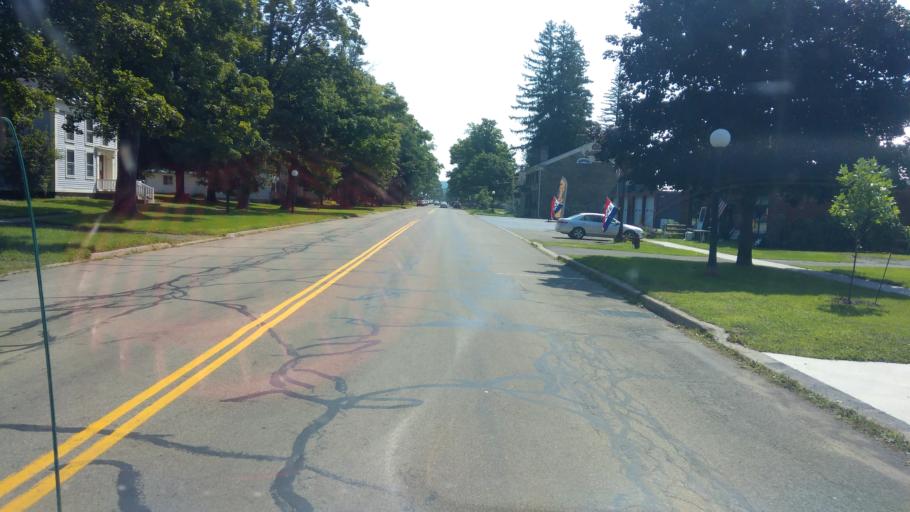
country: US
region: New York
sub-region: Allegany County
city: Belmont
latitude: 42.3076
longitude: -78.0214
